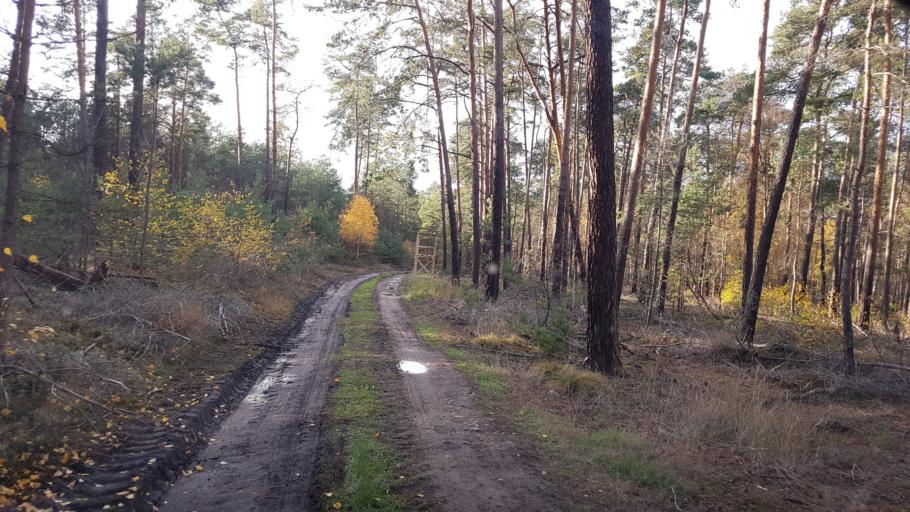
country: DE
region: Brandenburg
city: Trobitz
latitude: 51.6456
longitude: 13.4183
